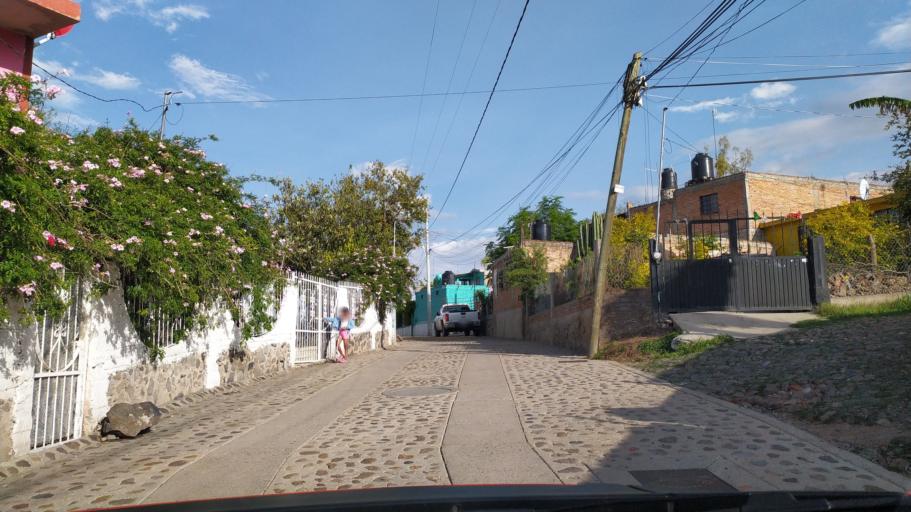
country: MX
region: Guanajuato
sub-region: San Francisco del Rincon
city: San Ignacio de Hidalgo
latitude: 20.9281
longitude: -101.9195
